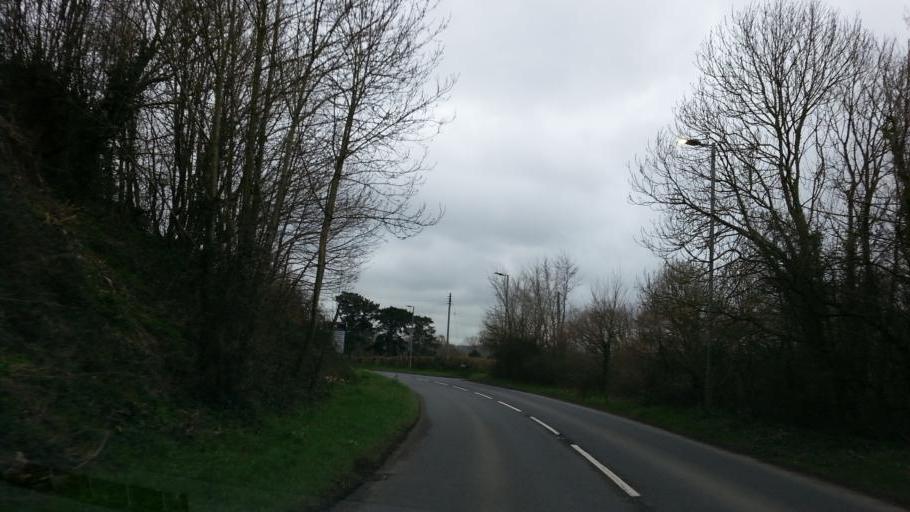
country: GB
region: England
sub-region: Devon
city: Barnstaple
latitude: 51.0964
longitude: -4.0557
